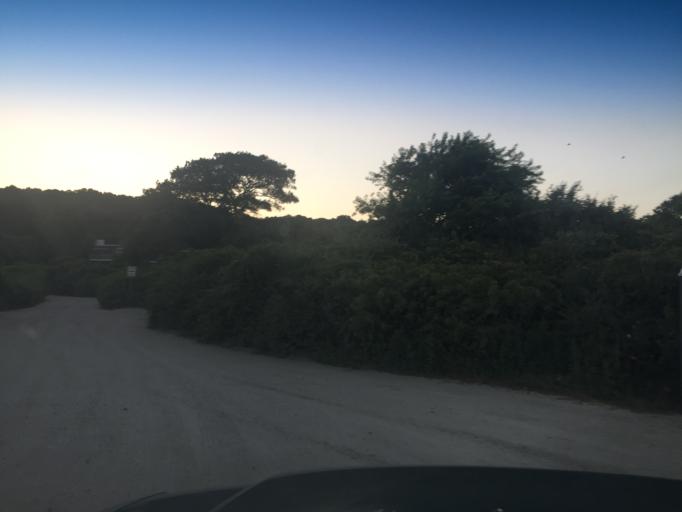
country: US
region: Massachusetts
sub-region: Barnstable County
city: Falmouth
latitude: 41.5347
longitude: -70.6420
